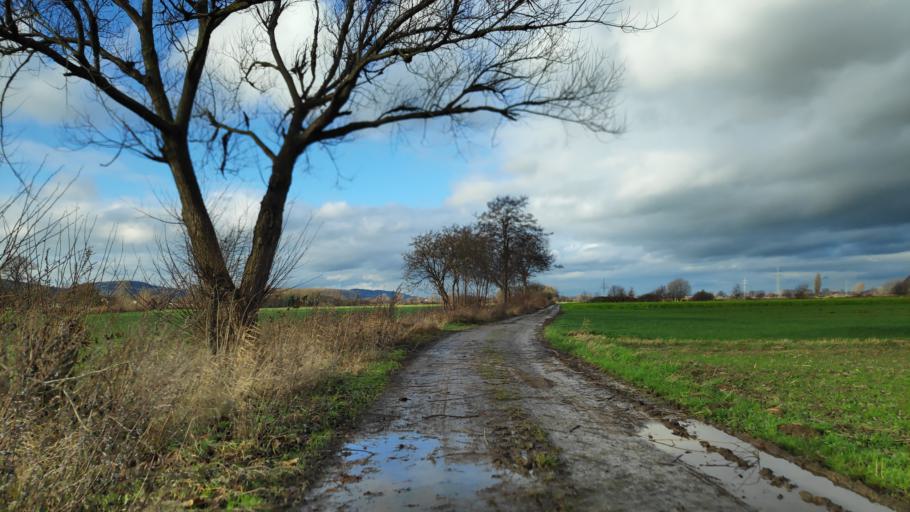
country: DE
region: North Rhine-Westphalia
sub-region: Regierungsbezirk Detmold
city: Minden
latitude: 52.2802
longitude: 8.8455
